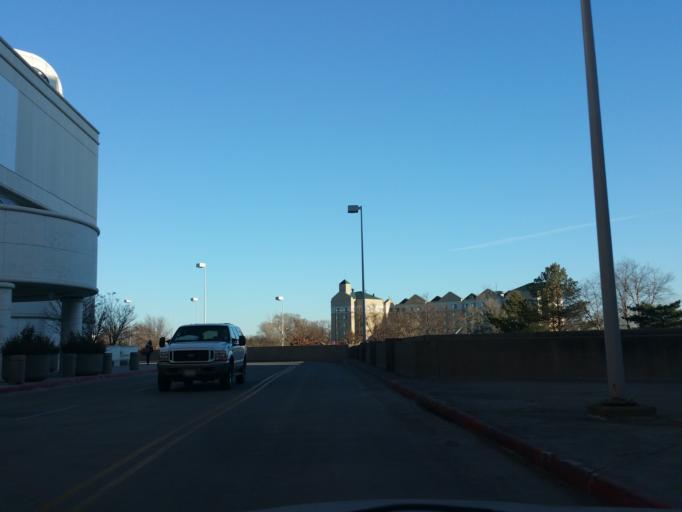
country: US
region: Minnesota
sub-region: Hennepin County
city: Richfield
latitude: 44.8532
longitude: -93.2407
